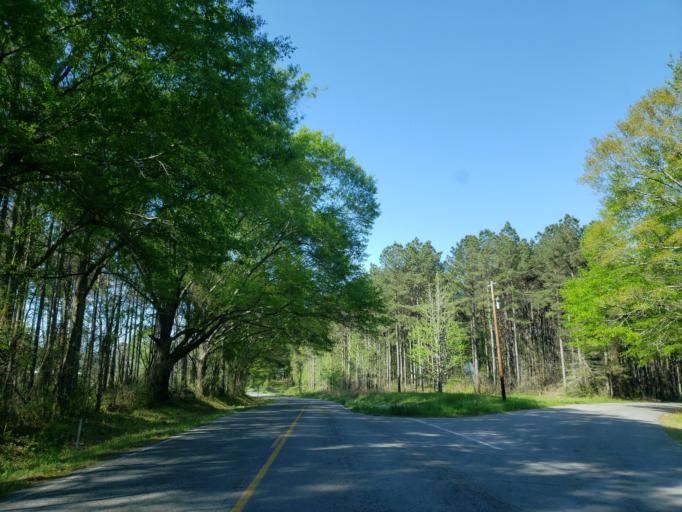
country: US
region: Mississippi
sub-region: Forrest County
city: Rawls Springs
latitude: 31.5127
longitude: -89.3592
